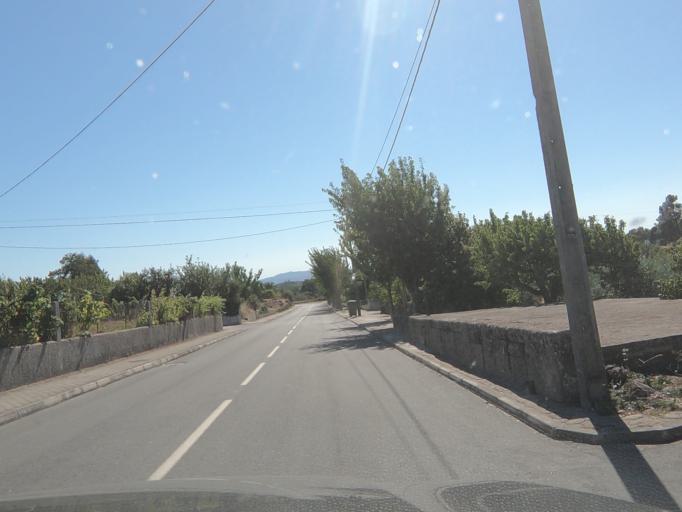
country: PT
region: Vila Real
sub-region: Valpacos
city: Valpacos
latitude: 41.6585
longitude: -7.3203
